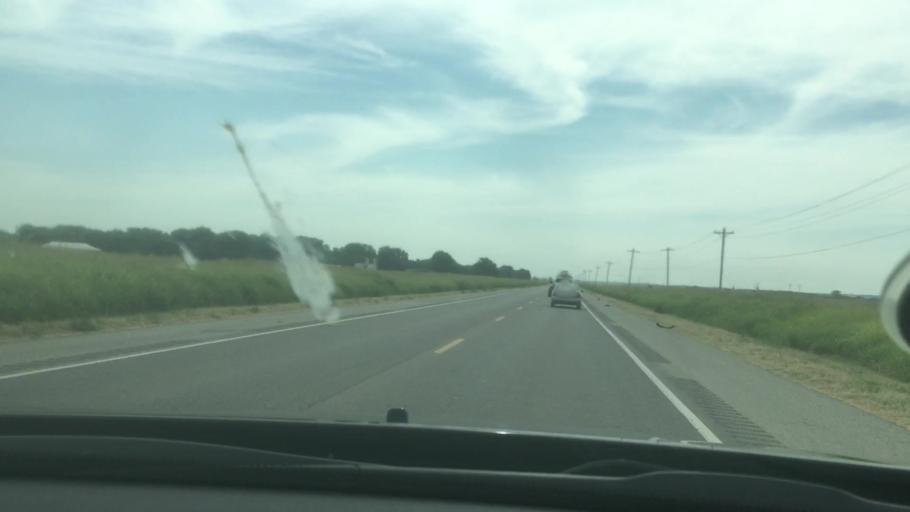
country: US
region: Oklahoma
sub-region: Garvin County
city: Lindsay
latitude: 34.8240
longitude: -97.5348
